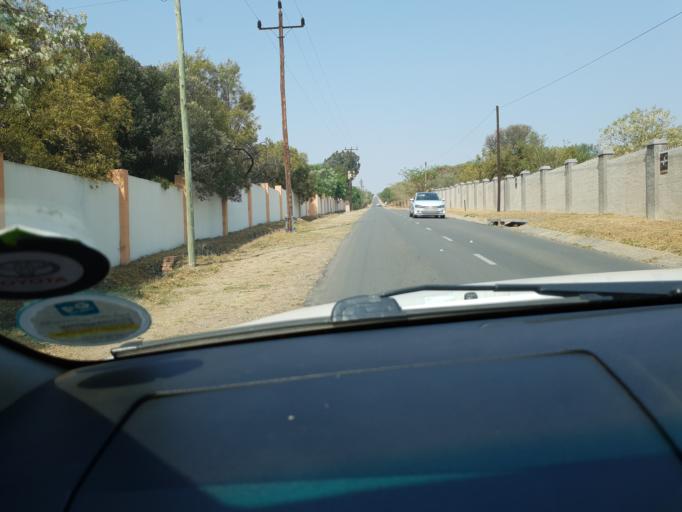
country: ZA
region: Gauteng
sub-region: City of Johannesburg Metropolitan Municipality
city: Midrand
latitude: -25.9902
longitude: 28.0974
